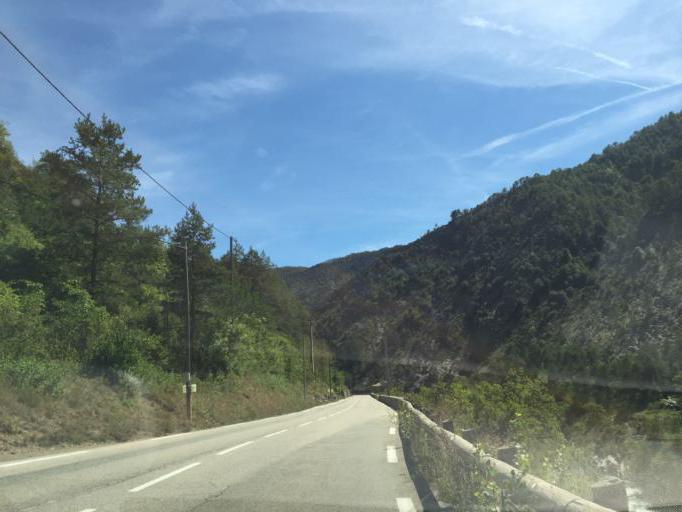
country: FR
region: Provence-Alpes-Cote d'Azur
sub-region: Departement des Alpes-Maritimes
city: Gilette
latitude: 43.9501
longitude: 7.1603
